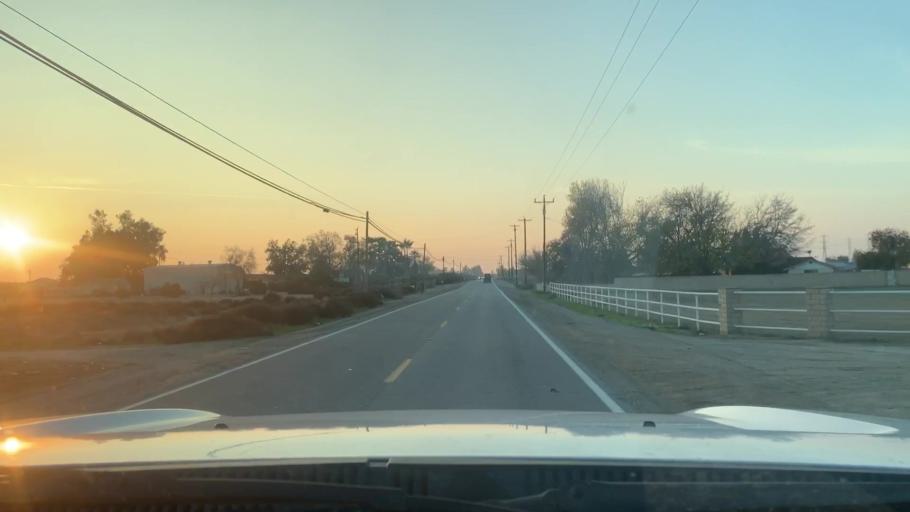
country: US
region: California
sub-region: Kern County
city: Rosedale
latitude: 35.3835
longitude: -119.1922
